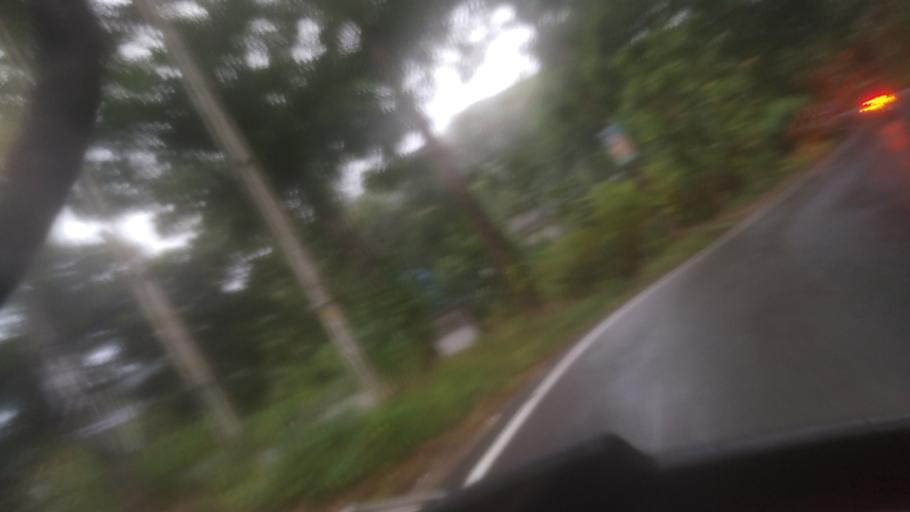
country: IN
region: Kerala
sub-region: Idukki
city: Idukki
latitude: 9.9284
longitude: 77.0728
